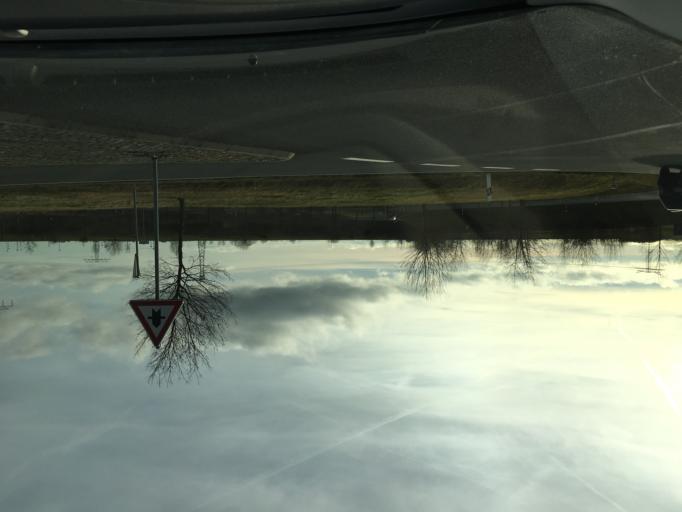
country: DE
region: Thuringia
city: Gerstenberg
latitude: 51.0222
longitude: 12.4581
